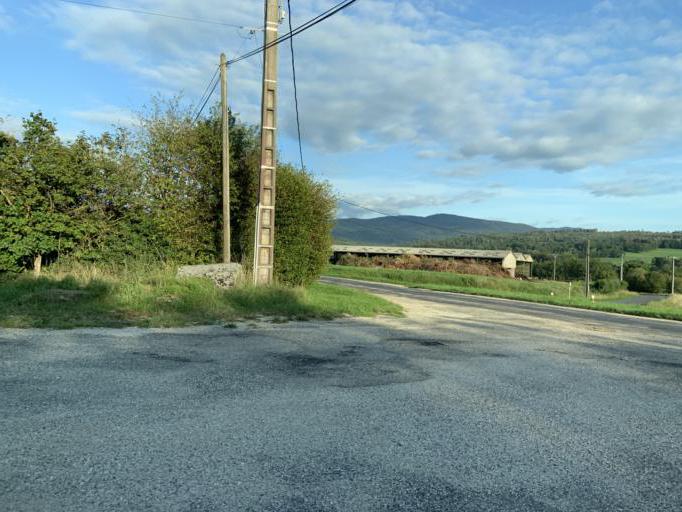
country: FR
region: Rhone-Alpes
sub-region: Departement de l'Ain
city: Dortan
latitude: 46.3009
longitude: 5.6351
